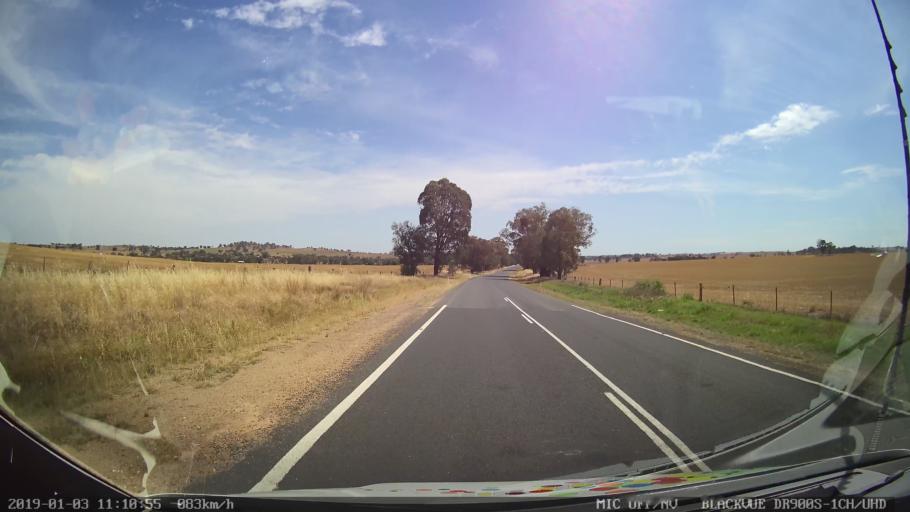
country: AU
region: New South Wales
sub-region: Young
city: Young
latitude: -34.2213
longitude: 148.2590
